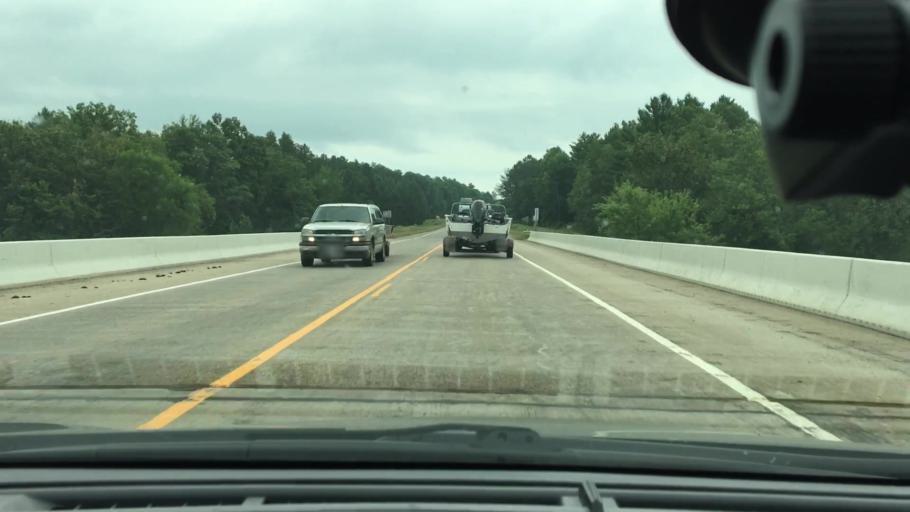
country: US
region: Minnesota
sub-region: Crow Wing County
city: Crosby
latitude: 46.5444
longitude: -93.9564
